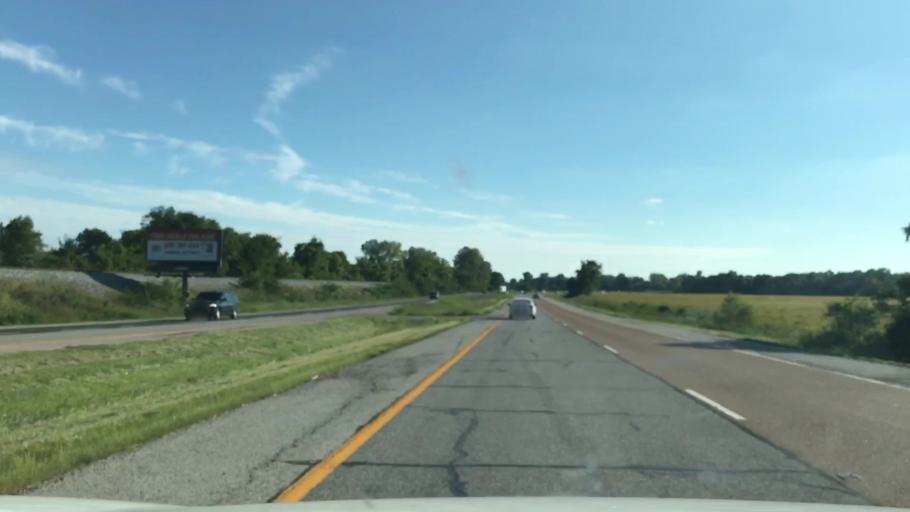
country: US
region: Illinois
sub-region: Madison County
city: Mitchell
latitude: 38.7864
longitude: -90.1068
